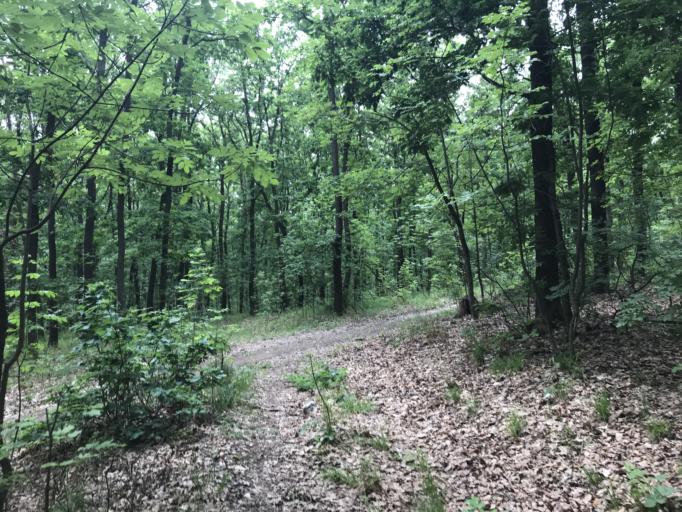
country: HU
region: Pest
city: Csobanka
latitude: 47.6562
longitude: 18.9344
